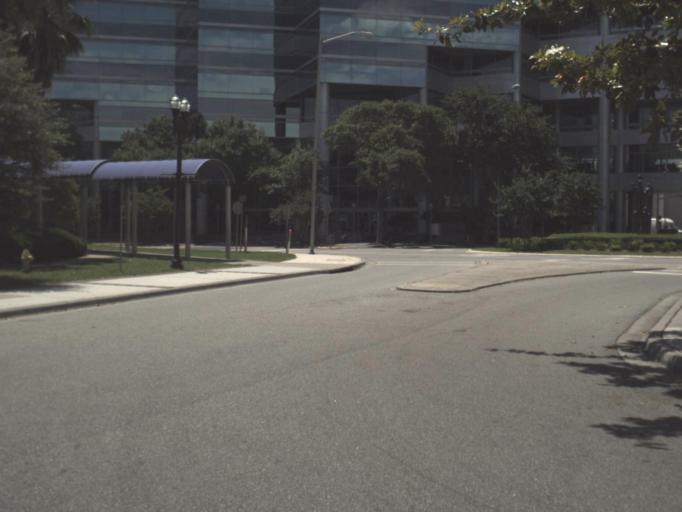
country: US
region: Florida
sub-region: Duval County
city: Jacksonville
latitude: 30.3191
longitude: -81.6606
